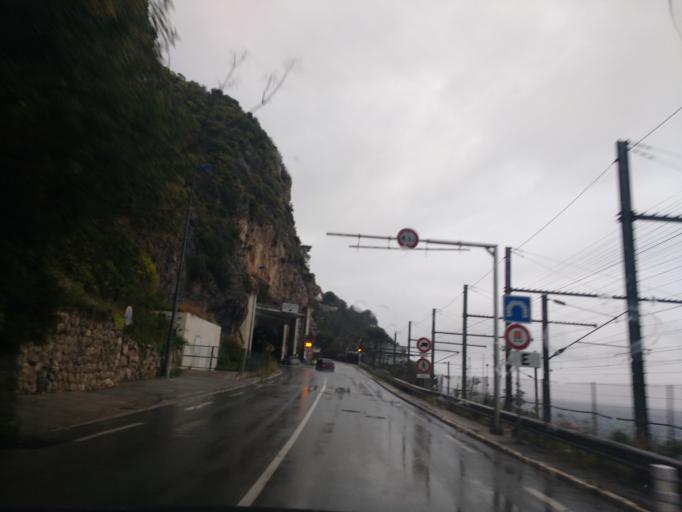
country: FR
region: Provence-Alpes-Cote d'Azur
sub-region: Departement des Alpes-Maritimes
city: Eze
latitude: 43.7208
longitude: 7.3677
